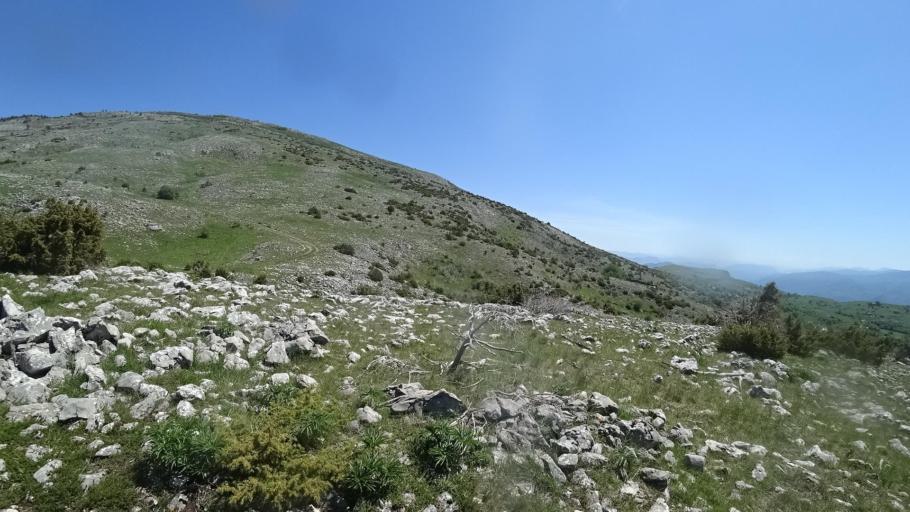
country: BA
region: Federation of Bosnia and Herzegovina
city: Rumboci
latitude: 43.8372
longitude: 17.4428
